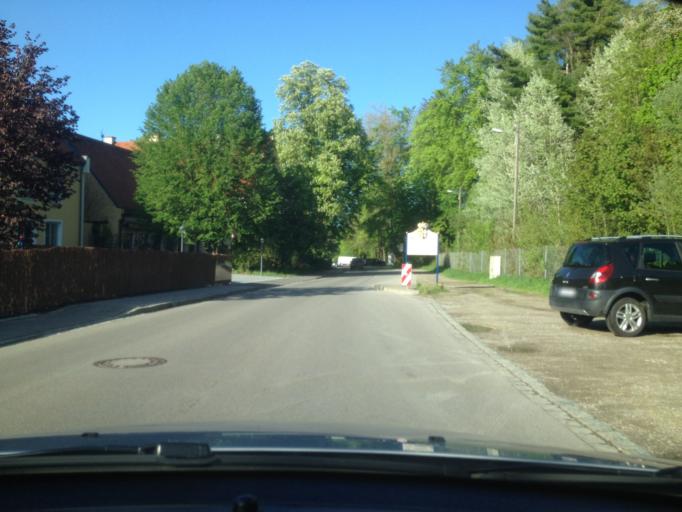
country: DE
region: Bavaria
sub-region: Swabia
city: Stadtbergen
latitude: 48.3338
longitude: 10.8256
